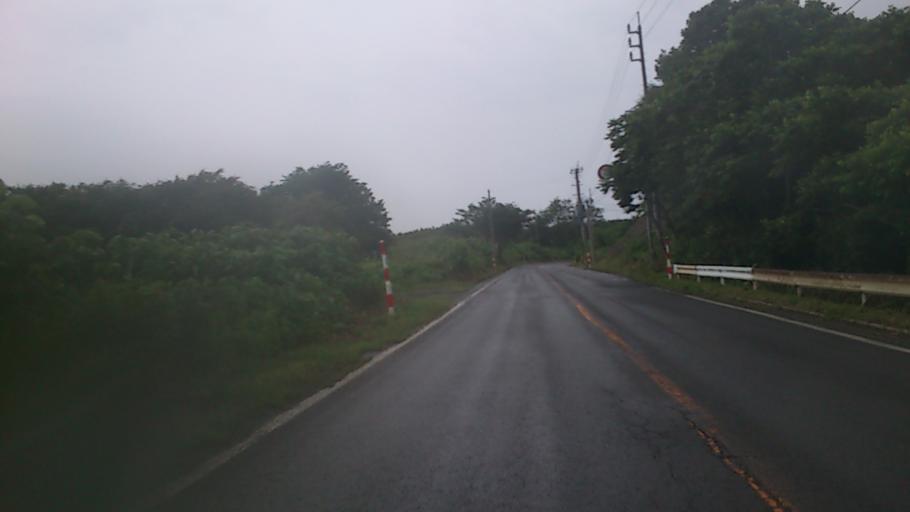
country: JP
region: Akita
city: Noshiromachi
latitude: 40.4250
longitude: 139.9452
